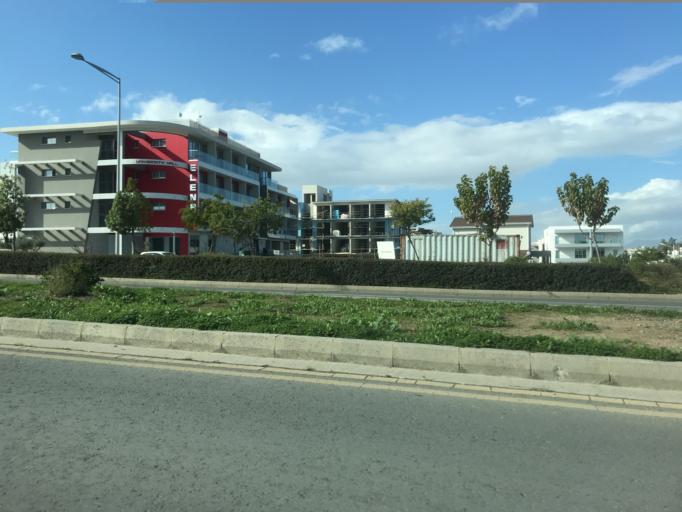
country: CY
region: Lefkosia
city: Geri
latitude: 35.1485
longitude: 33.4105
